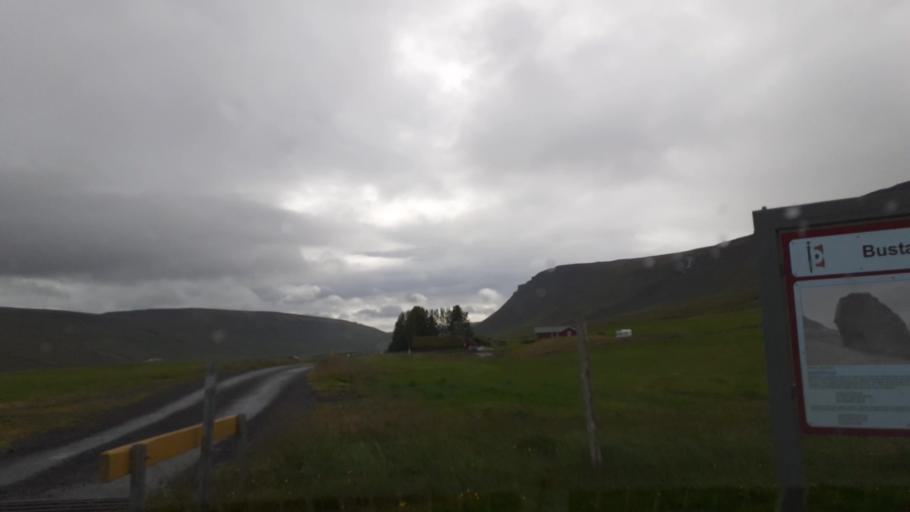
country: IS
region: East
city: Egilsstadir
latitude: 65.6172
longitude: -15.0952
